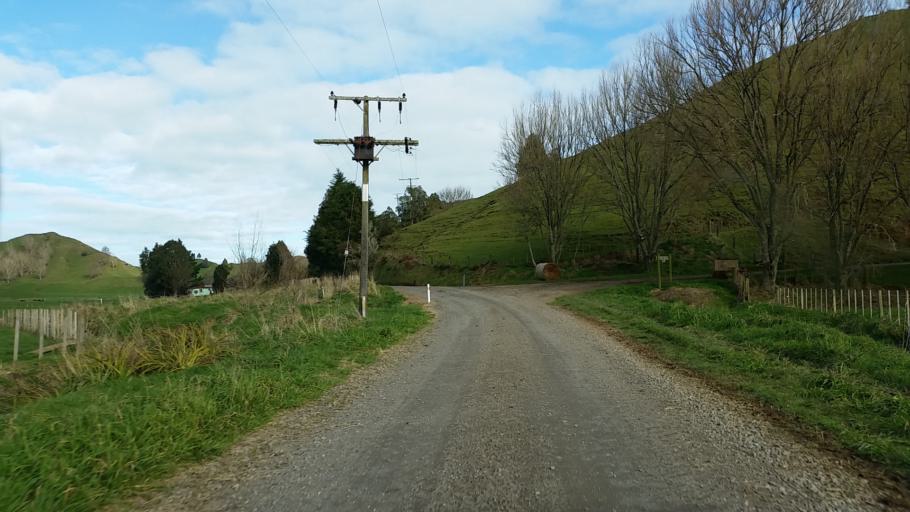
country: NZ
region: Taranaki
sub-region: South Taranaki District
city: Eltham
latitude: -39.2511
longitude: 174.5350
